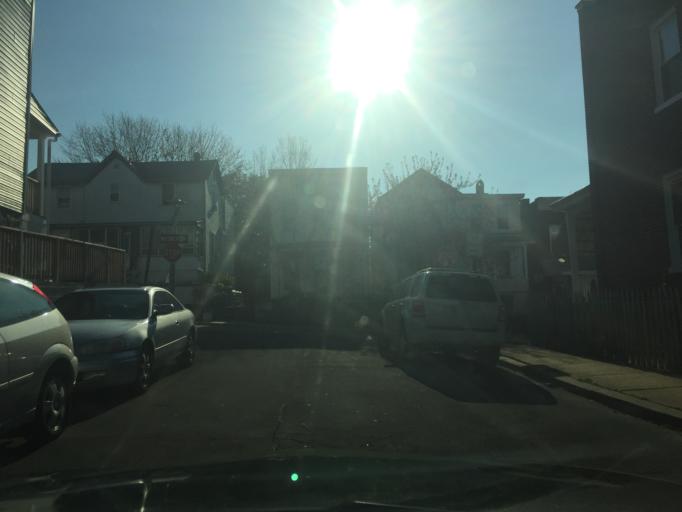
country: US
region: Maryland
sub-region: City of Baltimore
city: Baltimore
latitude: 39.3312
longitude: -76.6391
